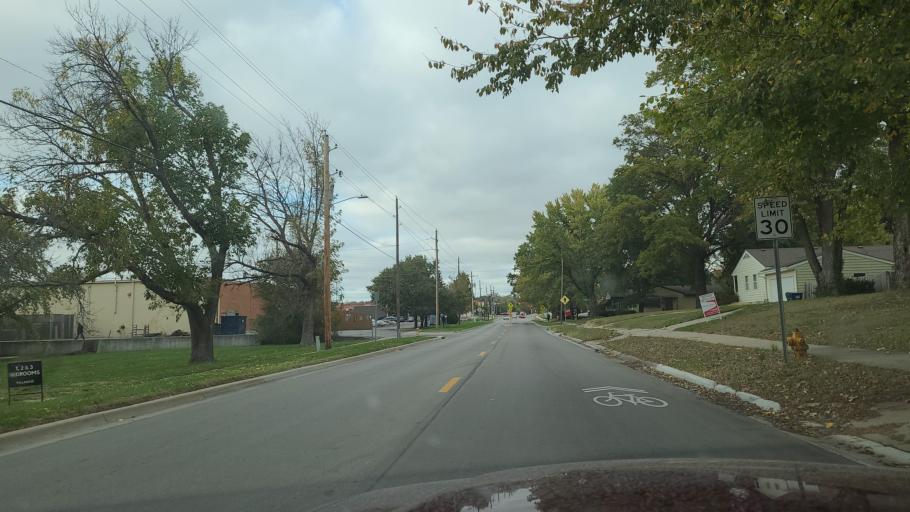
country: US
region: Kansas
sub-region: Douglas County
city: Lawrence
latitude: 38.9398
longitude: -95.2418
